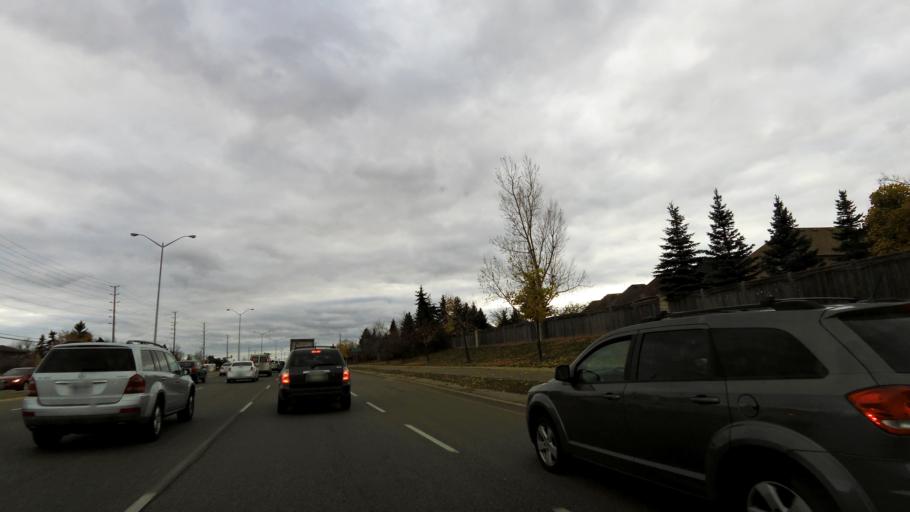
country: CA
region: Ontario
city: Brampton
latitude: 43.7396
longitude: -79.7496
